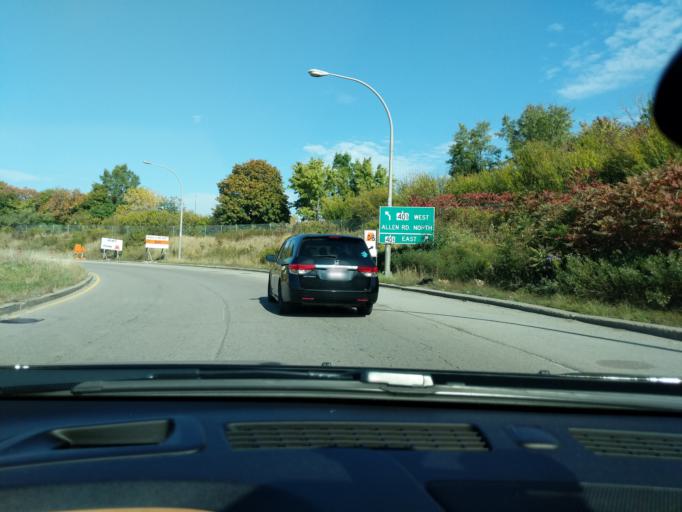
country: CA
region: Ontario
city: Toronto
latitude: 43.7260
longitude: -79.4467
